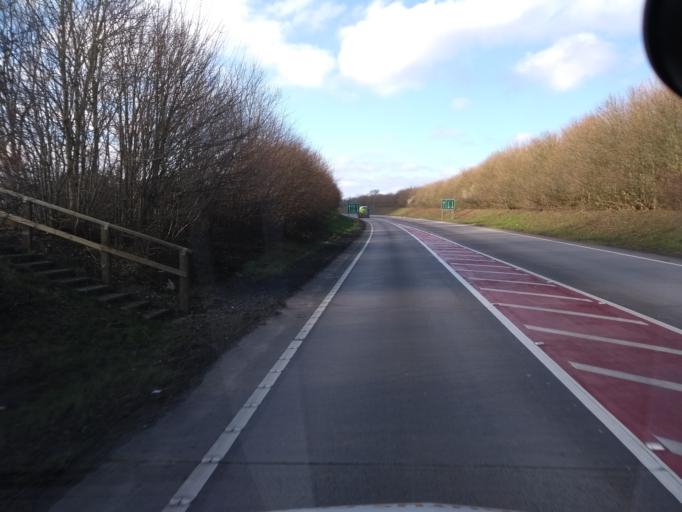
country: GB
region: England
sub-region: Somerset
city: South Petherton
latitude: 50.9373
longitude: -2.8464
